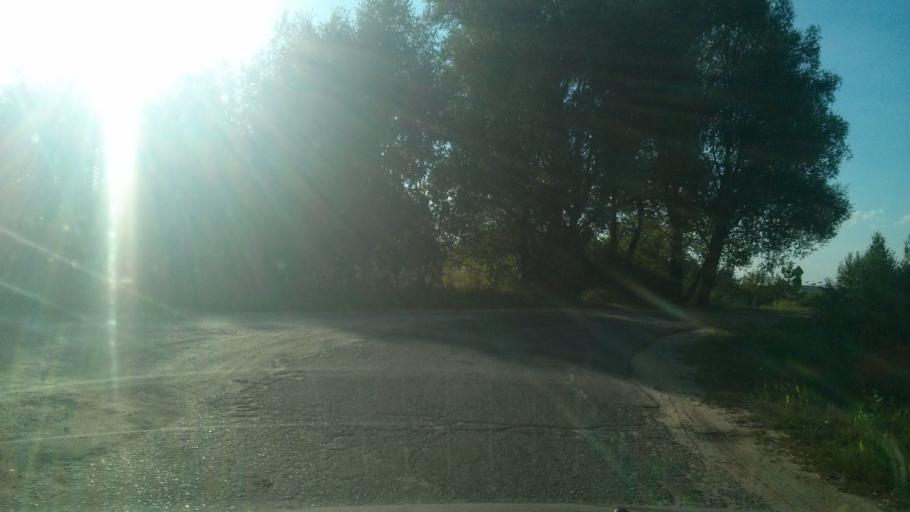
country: RU
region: Vladimir
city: Melenki
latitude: 55.2952
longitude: 41.7959
